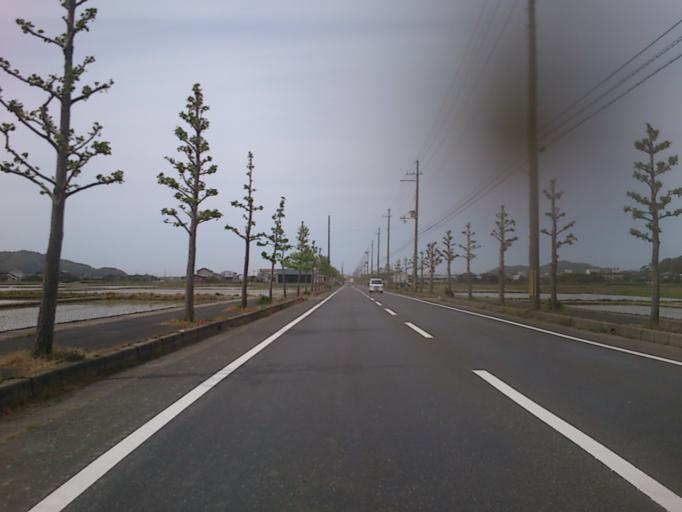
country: JP
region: Kyoto
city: Miyazu
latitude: 35.6701
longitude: 135.0250
